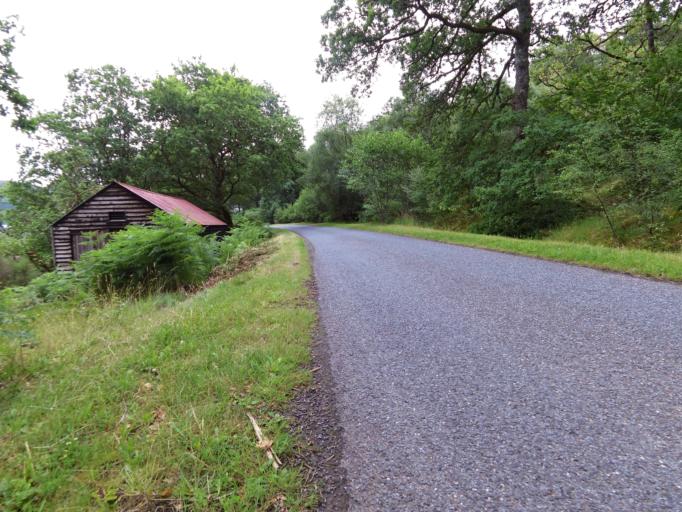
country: GB
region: Scotland
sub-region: Highland
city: Fort William
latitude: 56.8290
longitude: -5.1256
